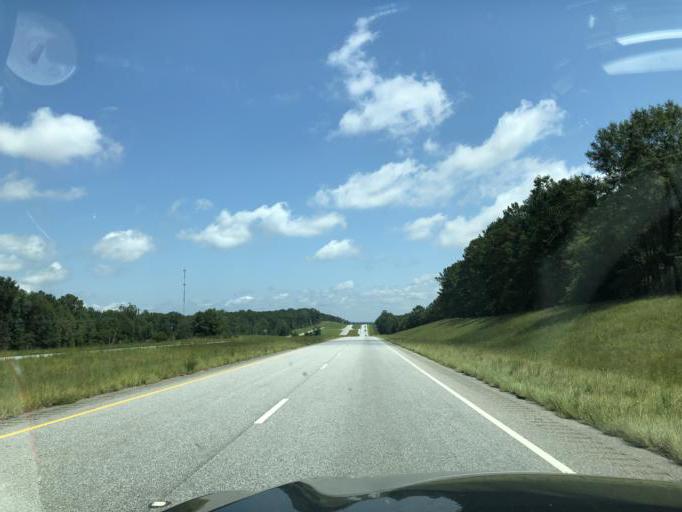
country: US
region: Alabama
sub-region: Barbour County
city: Eufaula
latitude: 31.7609
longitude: -85.2046
